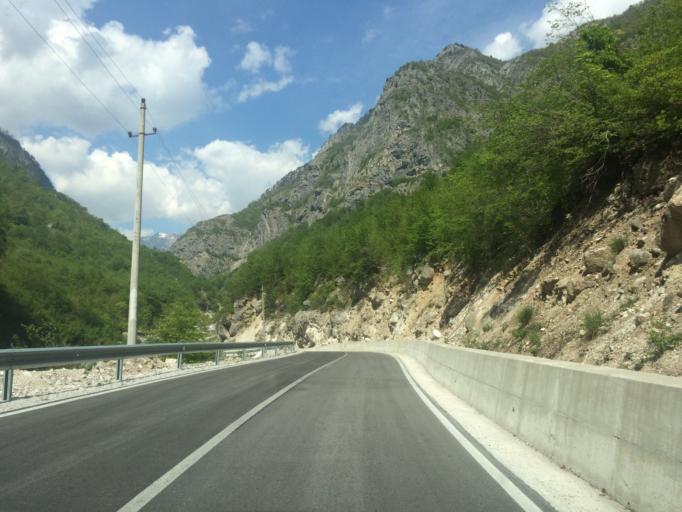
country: AL
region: Kukes
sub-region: Rrethi i Tropojes
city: Bajram Curri
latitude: 42.4093
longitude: 20.0249
